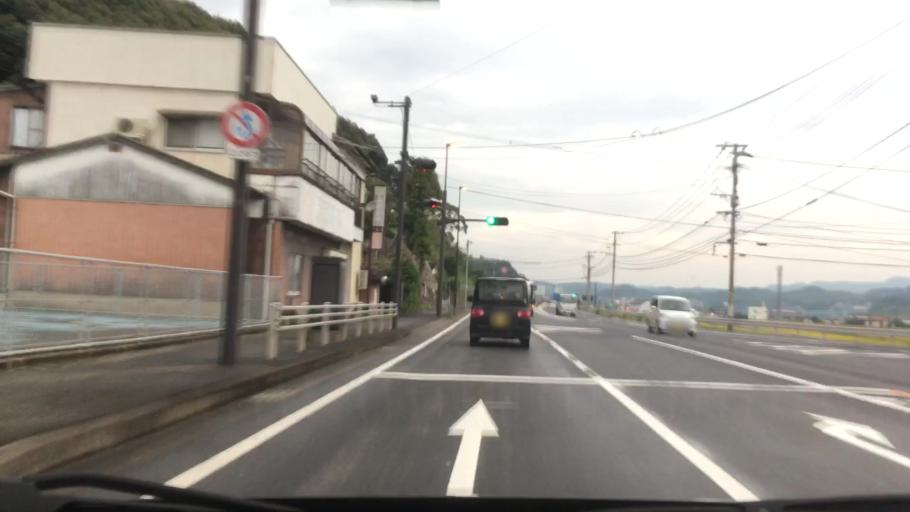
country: JP
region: Nagasaki
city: Sasebo
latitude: 33.1046
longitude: 129.7781
